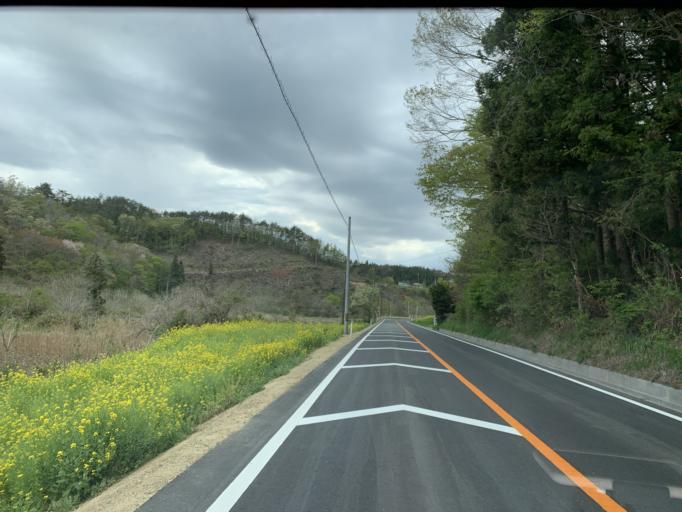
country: JP
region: Iwate
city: Ichinoseki
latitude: 38.7855
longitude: 141.4028
